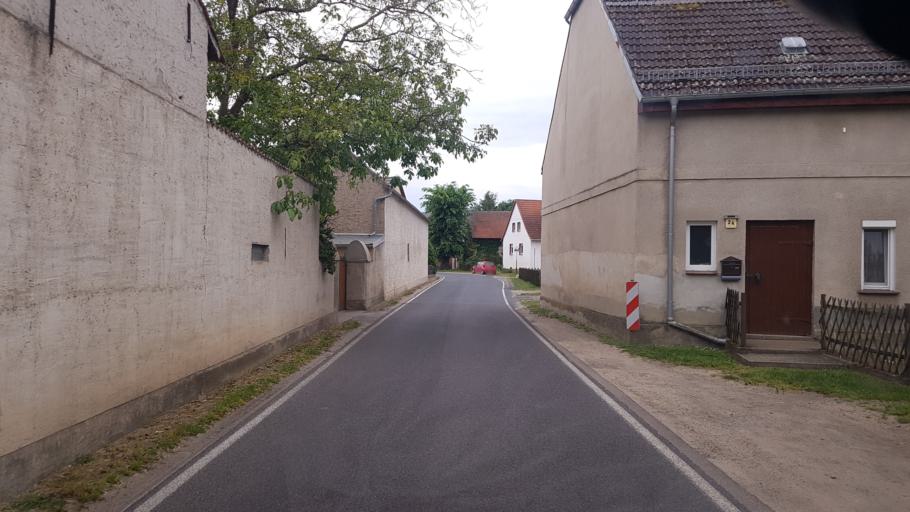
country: DE
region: Saxony-Anhalt
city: Holzdorf
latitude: 51.8007
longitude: 13.2368
